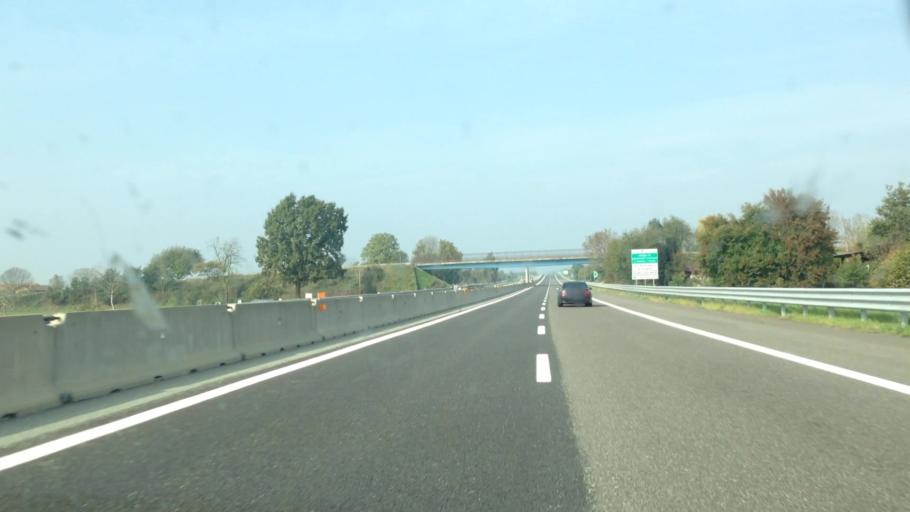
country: IT
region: Piedmont
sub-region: Provincia di Vercelli
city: Santhia
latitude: 45.3566
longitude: 8.1670
